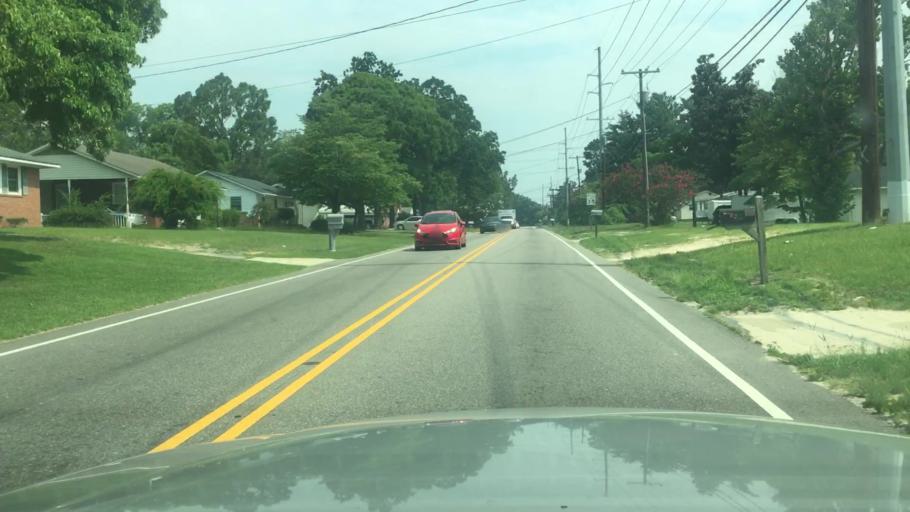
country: US
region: North Carolina
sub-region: Cumberland County
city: Hope Mills
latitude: 35.0176
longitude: -78.9401
